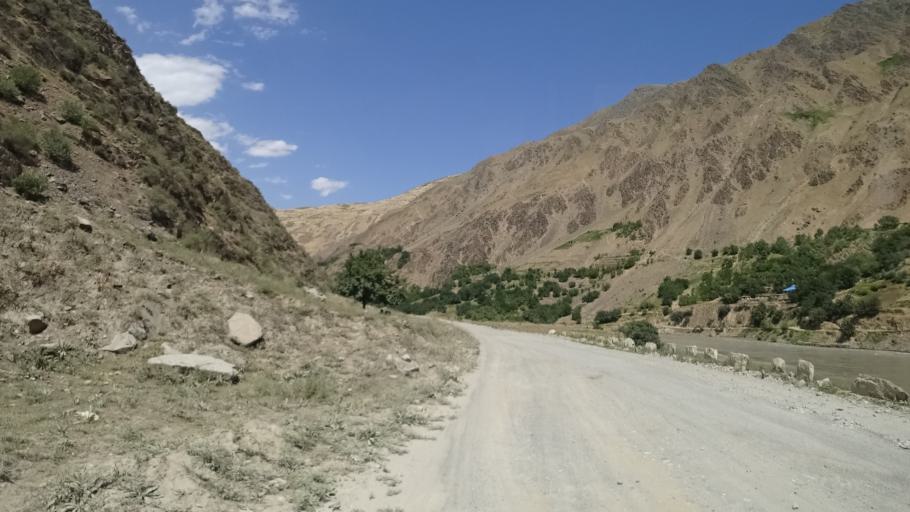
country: AF
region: Badakhshan
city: Maymay
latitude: 38.4393
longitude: 70.9543
